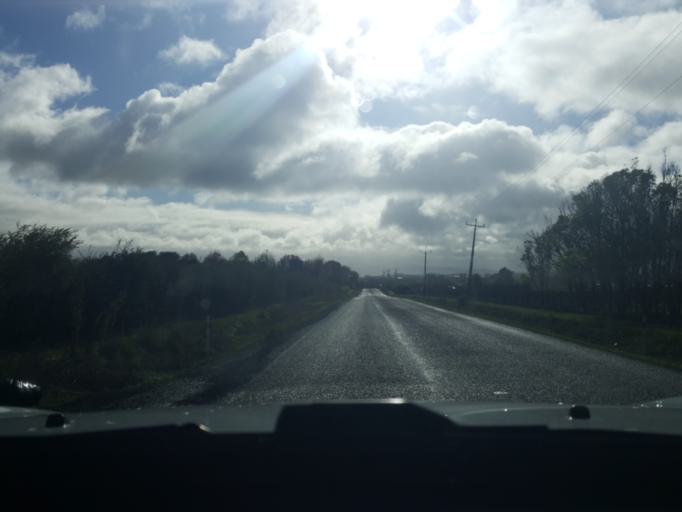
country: NZ
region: Auckland
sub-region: Auckland
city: Pukekohe East
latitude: -37.3097
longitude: 175.0090
